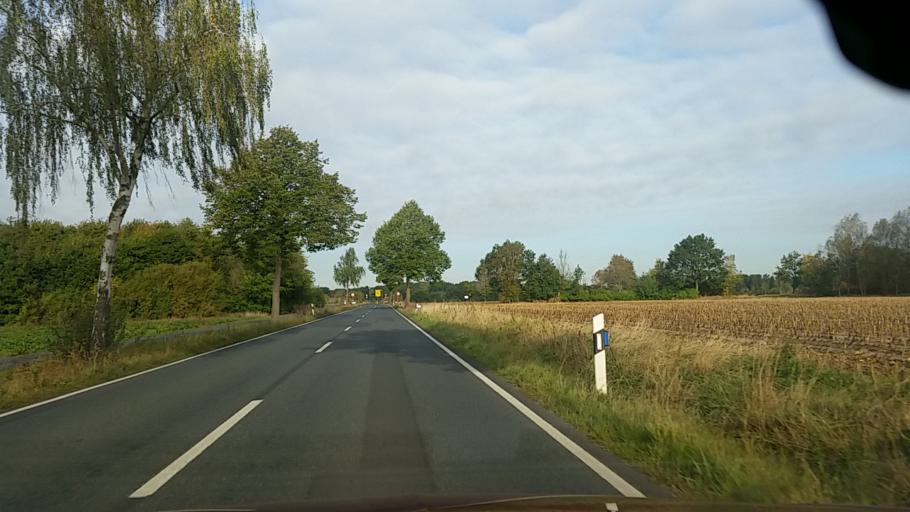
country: DE
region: Lower Saxony
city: Lachendorf
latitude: 52.6188
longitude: 10.2619
